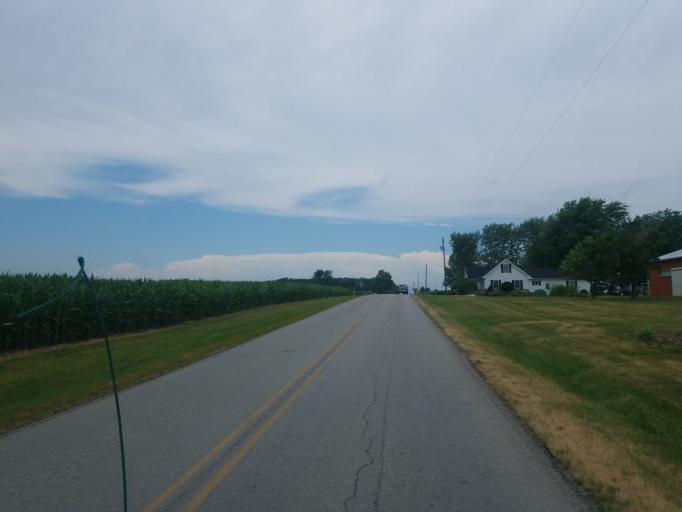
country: US
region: Indiana
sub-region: DeKalb County
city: Butler
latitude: 41.3858
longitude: -84.8734
